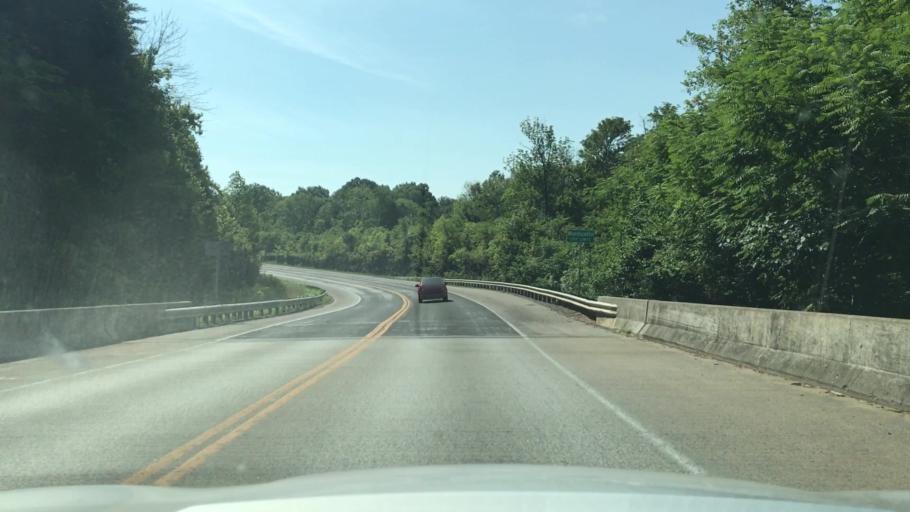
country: US
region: Kentucky
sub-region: Wayne County
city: Monticello
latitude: 36.8173
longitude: -84.8795
